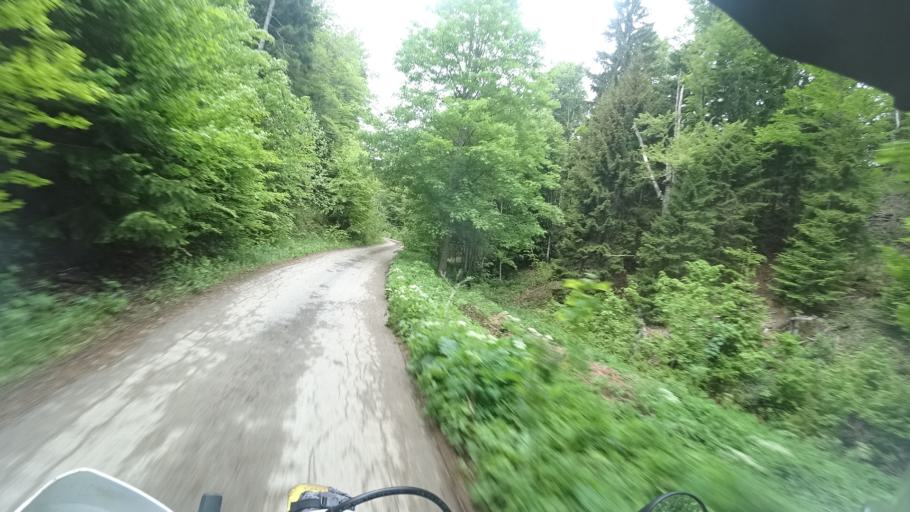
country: BA
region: Federation of Bosnia and Herzegovina
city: Bihac
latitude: 44.6721
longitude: 15.8466
